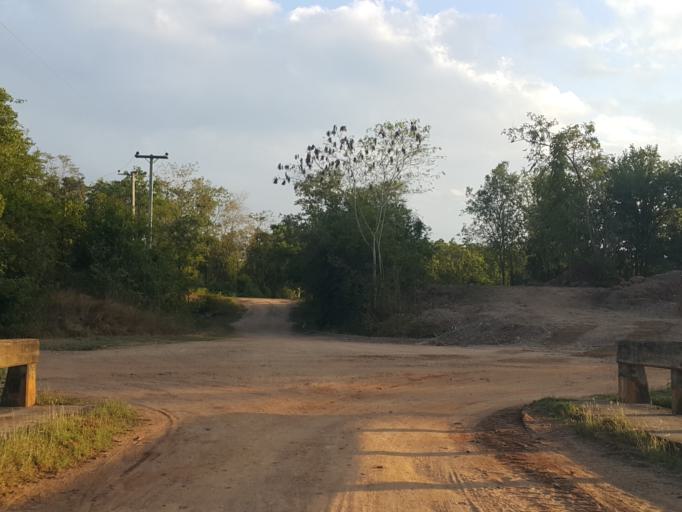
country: TH
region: Lampang
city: Lampang
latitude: 18.4342
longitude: 99.5822
